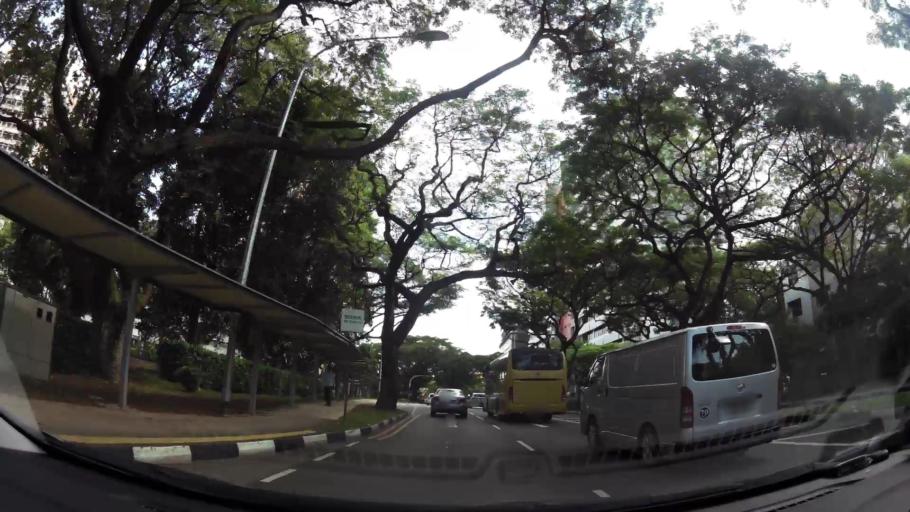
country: SG
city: Singapore
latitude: 1.2815
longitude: 103.8185
